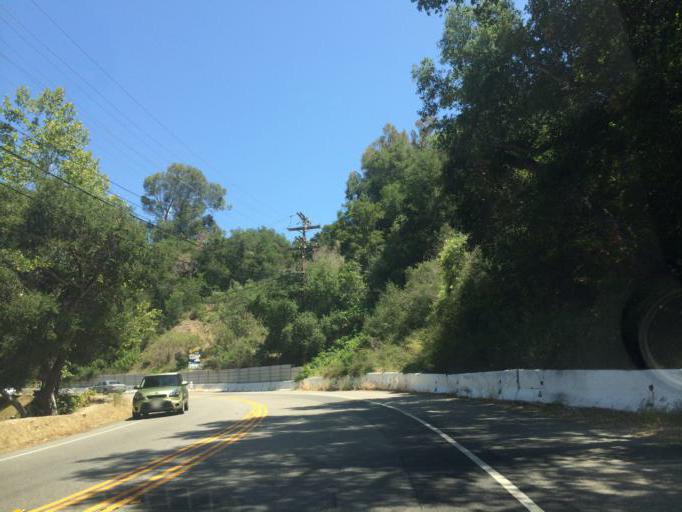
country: US
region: California
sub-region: Los Angeles County
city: Topanga
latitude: 34.1012
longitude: -118.5956
